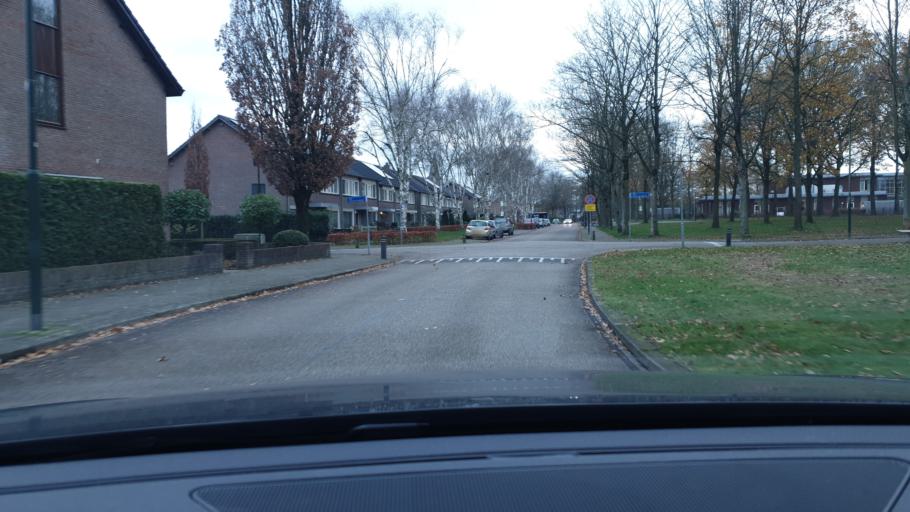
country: NL
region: North Brabant
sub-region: Gemeente Waalre
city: Waalre
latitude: 51.3897
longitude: 5.4398
